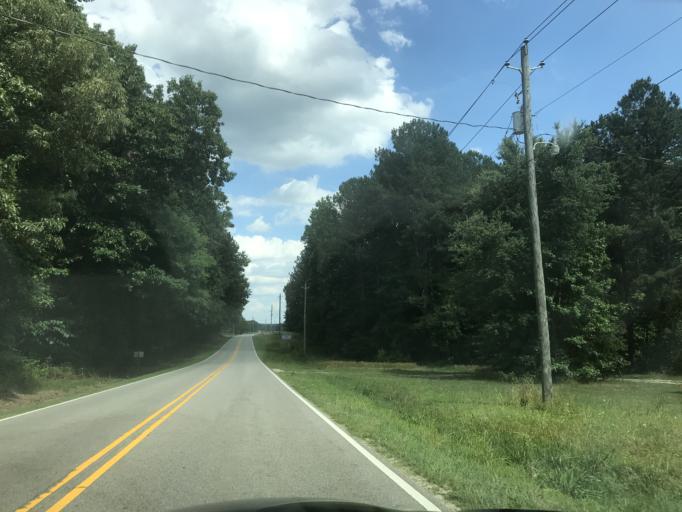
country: US
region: North Carolina
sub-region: Nash County
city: Spring Hope
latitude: 35.9457
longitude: -78.2280
